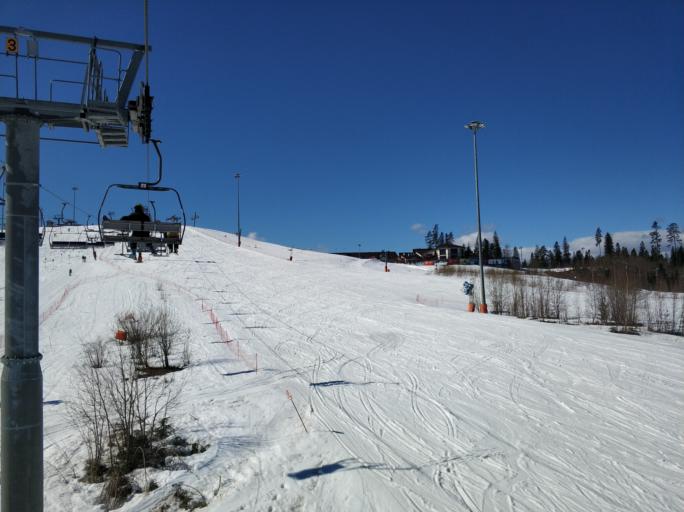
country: RU
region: Leningrad
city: Sosnovo
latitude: 60.5158
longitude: 30.2185
